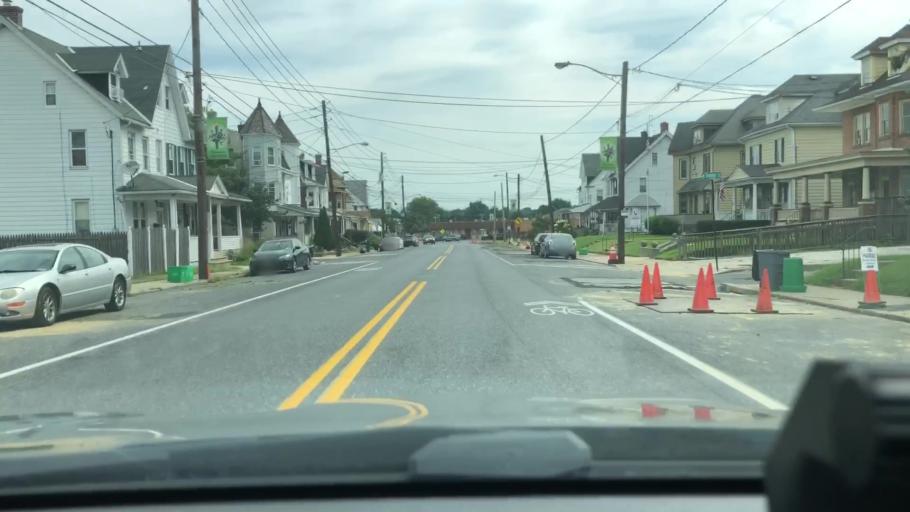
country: US
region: Pennsylvania
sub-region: Lehigh County
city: Fountain Hill
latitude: 40.6223
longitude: -75.4245
